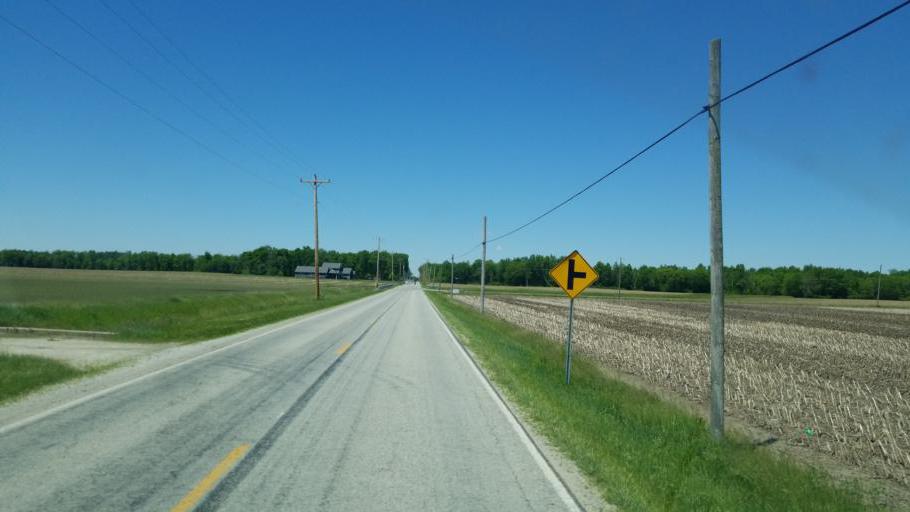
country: US
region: Ohio
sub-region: Shelby County
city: Fort Loramie
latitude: 40.3541
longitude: -84.3366
